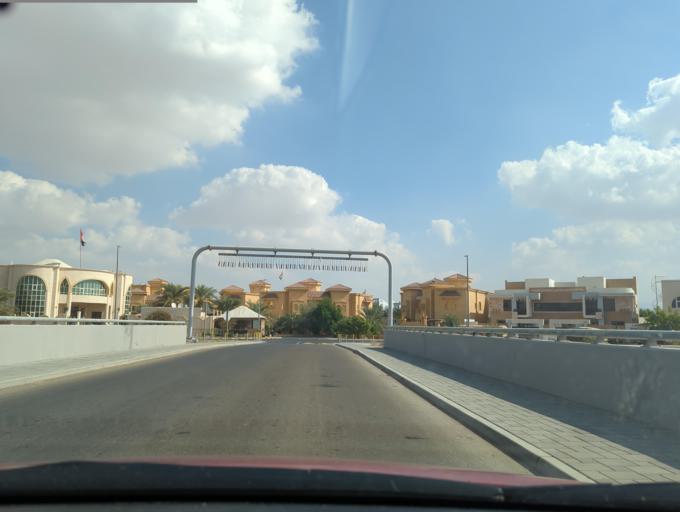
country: AE
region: Abu Dhabi
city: Al Ain
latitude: 24.1633
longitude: 55.6543
